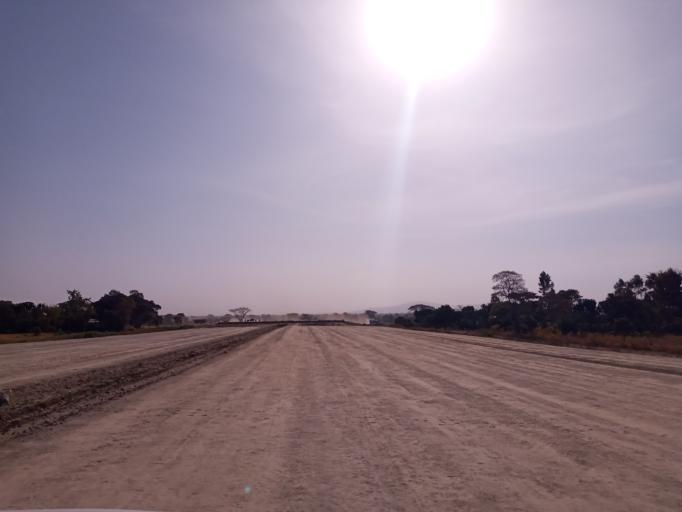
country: ET
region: Oromiya
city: Shashemene
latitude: 7.3106
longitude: 38.6234
